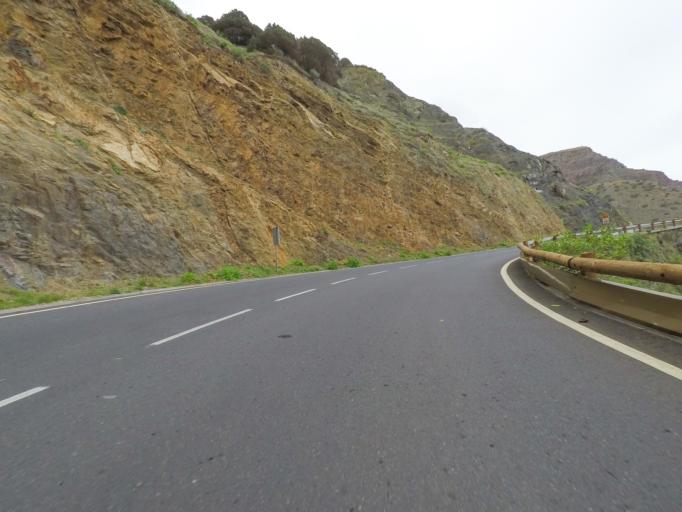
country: ES
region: Canary Islands
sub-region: Provincia de Santa Cruz de Tenerife
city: Agulo
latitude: 28.1907
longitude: -17.2025
